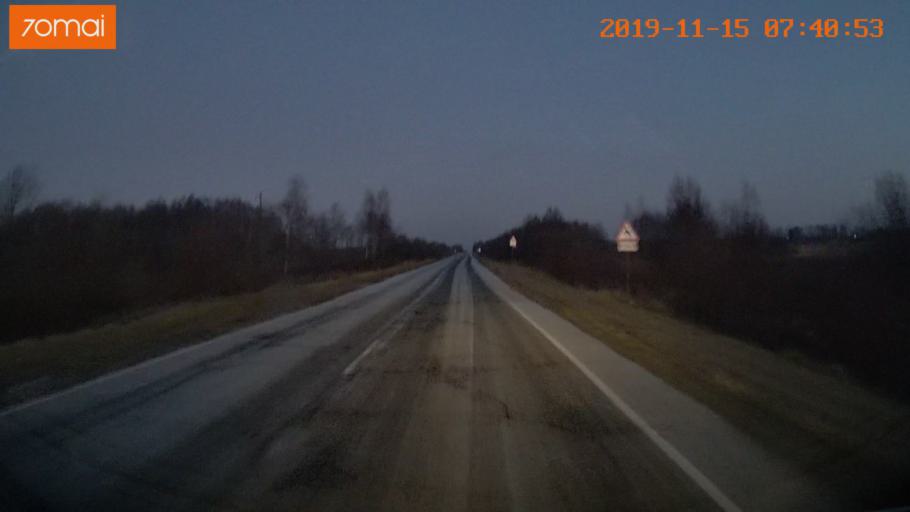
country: RU
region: Vologda
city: Sheksna
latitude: 58.7753
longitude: 38.3655
